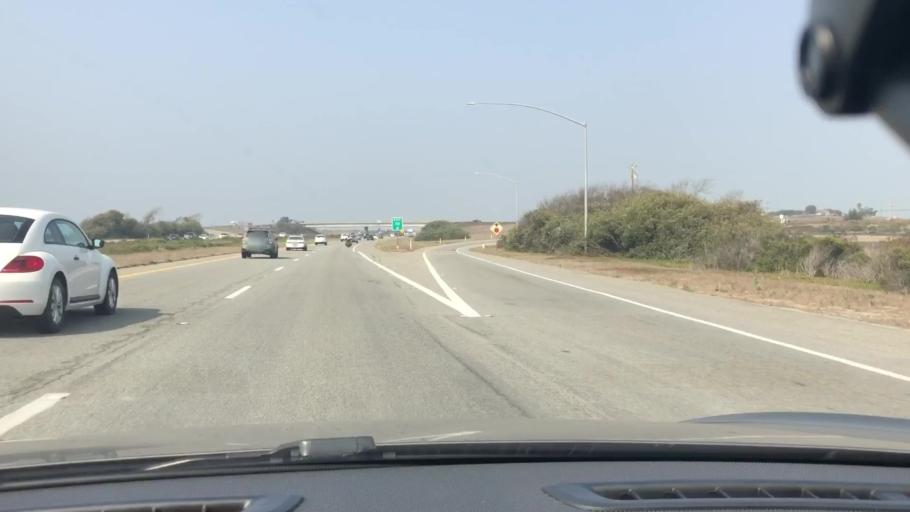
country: US
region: California
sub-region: Monterey County
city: Marina
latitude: 36.7213
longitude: -121.7919
